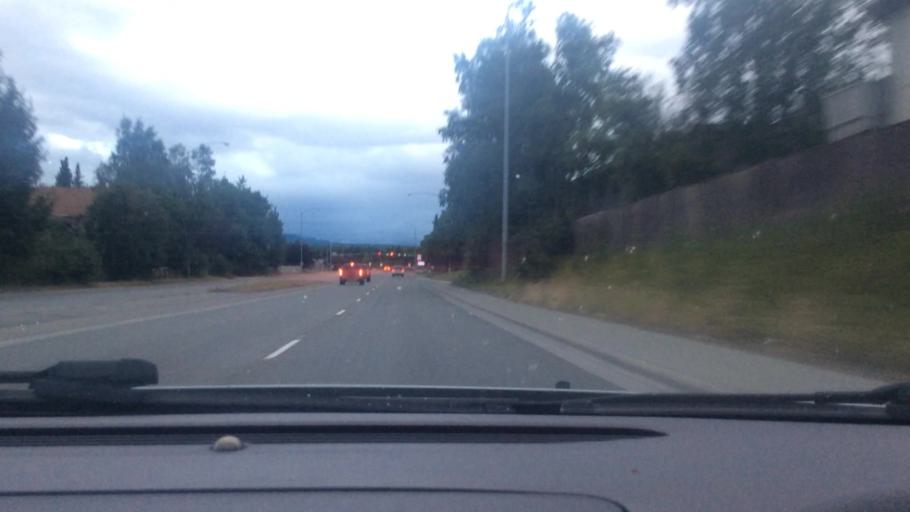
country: US
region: Alaska
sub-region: Anchorage Municipality
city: Anchorage
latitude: 61.1840
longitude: -149.7785
